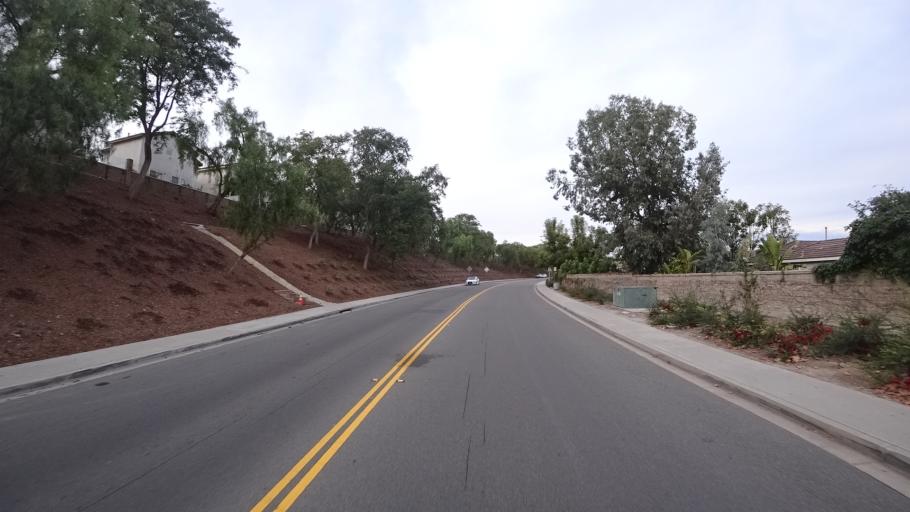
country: US
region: California
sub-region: Orange County
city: Aliso Viejo
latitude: 33.5770
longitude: -117.7336
